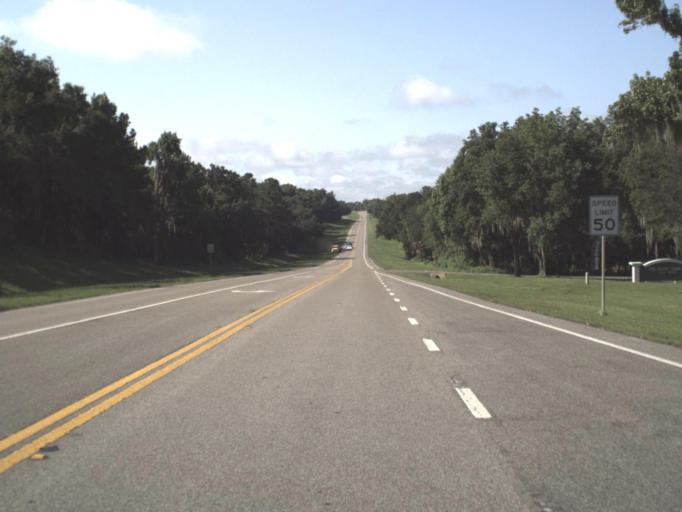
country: US
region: Florida
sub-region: Hernando County
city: North Brooksville
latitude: 28.5909
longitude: -82.4007
